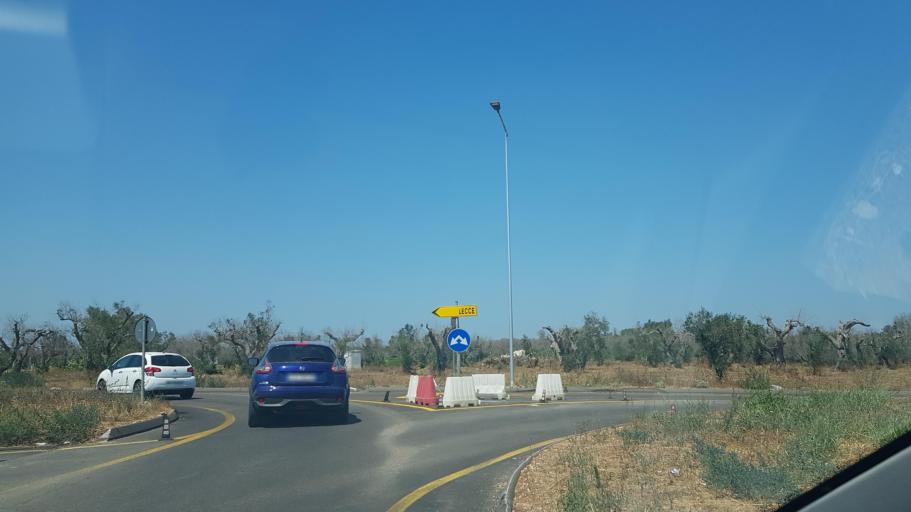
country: IT
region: Apulia
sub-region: Provincia di Lecce
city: Struda
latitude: 40.3247
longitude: 18.2599
